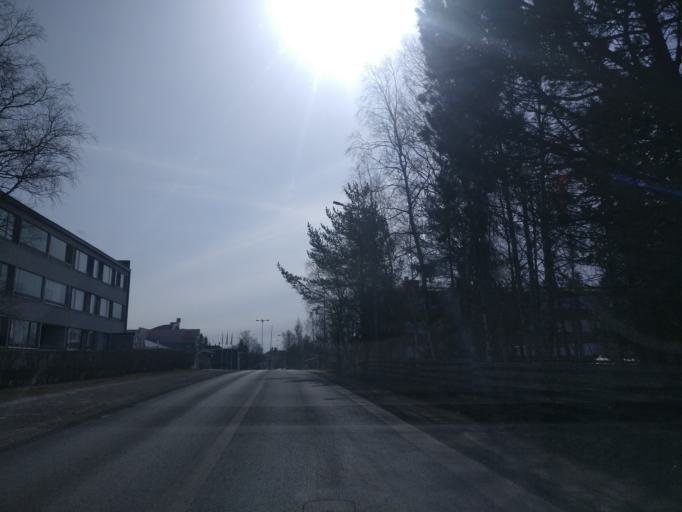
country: FI
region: Lapland
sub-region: Kemi-Tornio
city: Kemi
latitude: 65.7310
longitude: 24.5985
